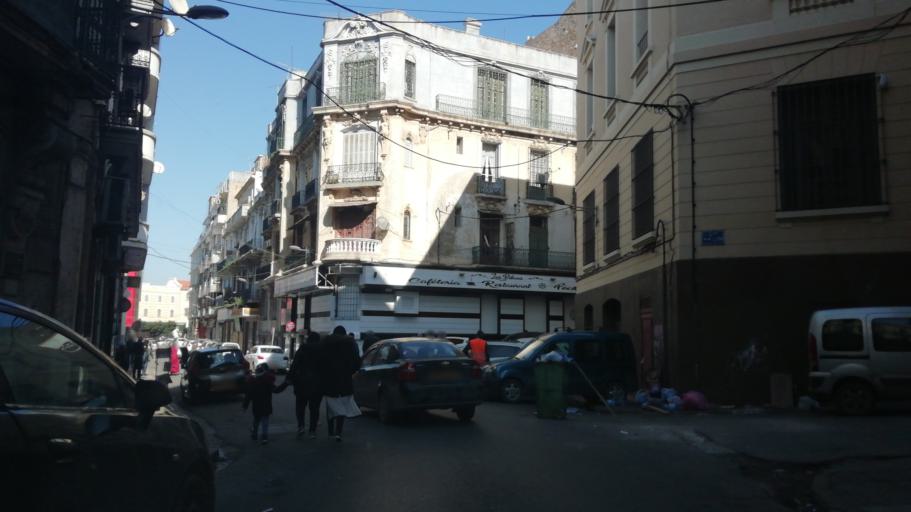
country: DZ
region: Oran
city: Oran
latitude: 35.7029
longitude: -0.6460
